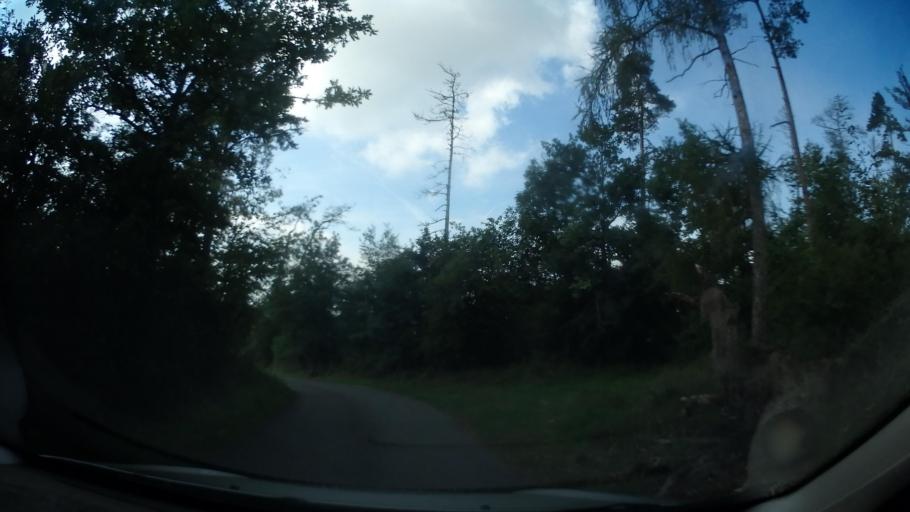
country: CZ
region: Central Bohemia
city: Novy Knin
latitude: 49.6997
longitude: 14.3245
